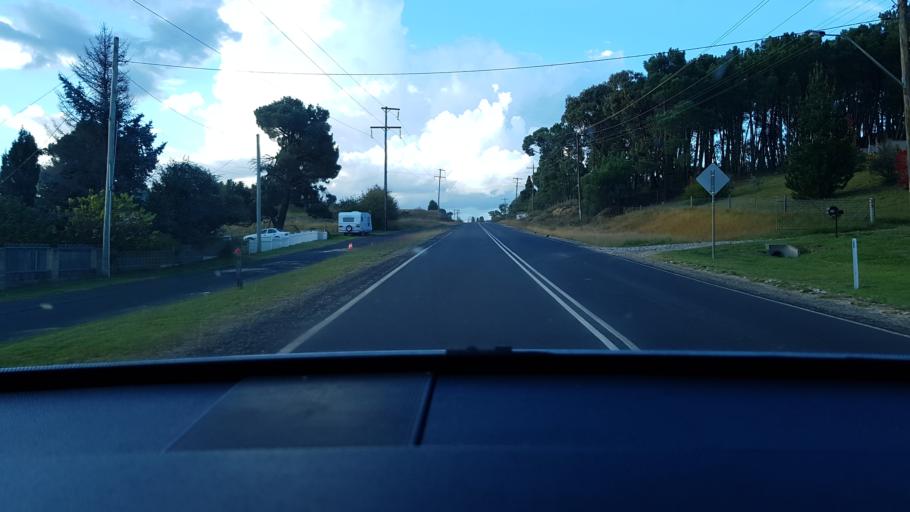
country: AU
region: New South Wales
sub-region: Lithgow
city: Lithgow
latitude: -33.3947
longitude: 150.0835
